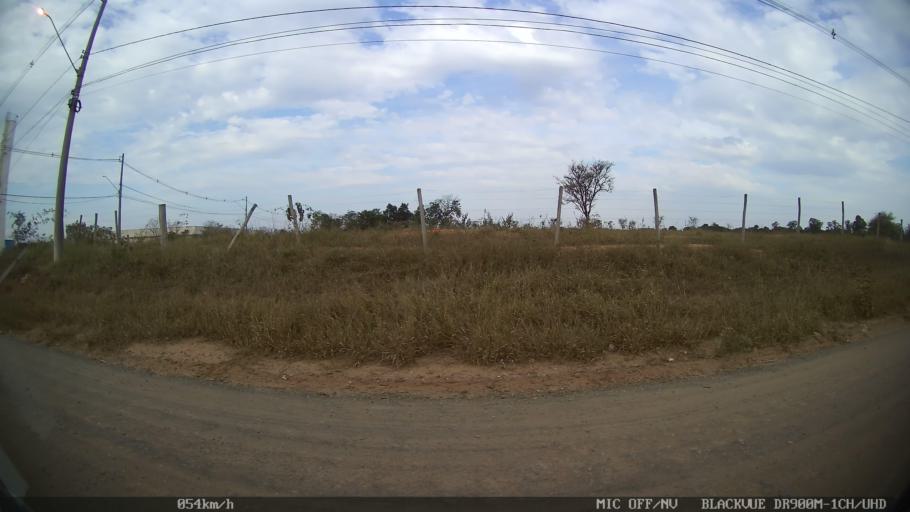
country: BR
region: Sao Paulo
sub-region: Paulinia
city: Paulinia
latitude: -22.7196
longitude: -47.1591
